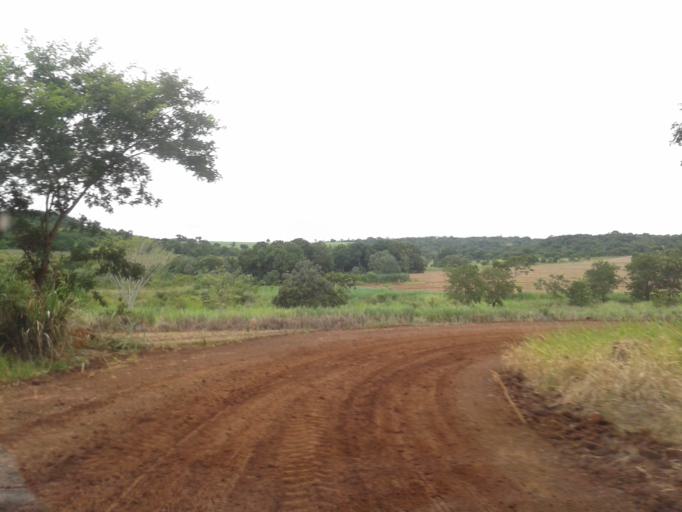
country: BR
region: Minas Gerais
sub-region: Capinopolis
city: Capinopolis
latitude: -18.7253
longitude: -49.7683
